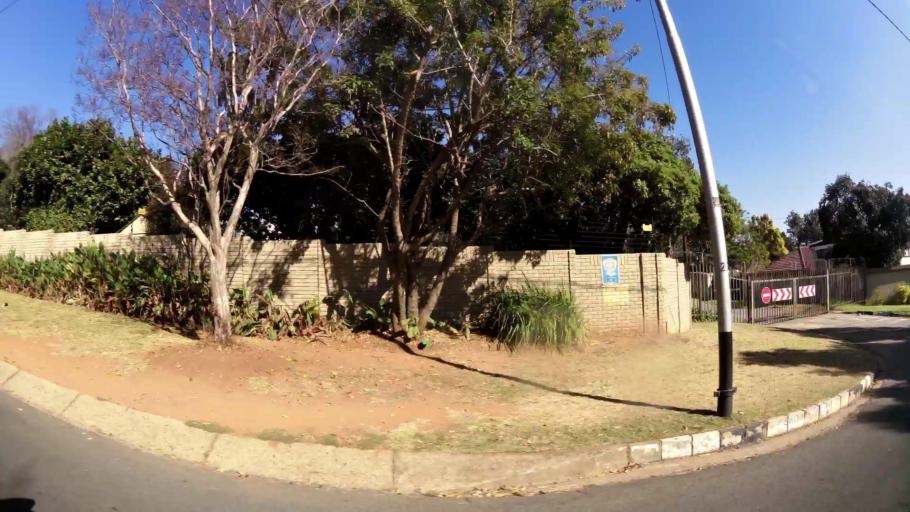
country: ZA
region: Gauteng
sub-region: City of Johannesburg Metropolitan Municipality
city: Modderfontein
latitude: -26.1331
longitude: 28.1111
